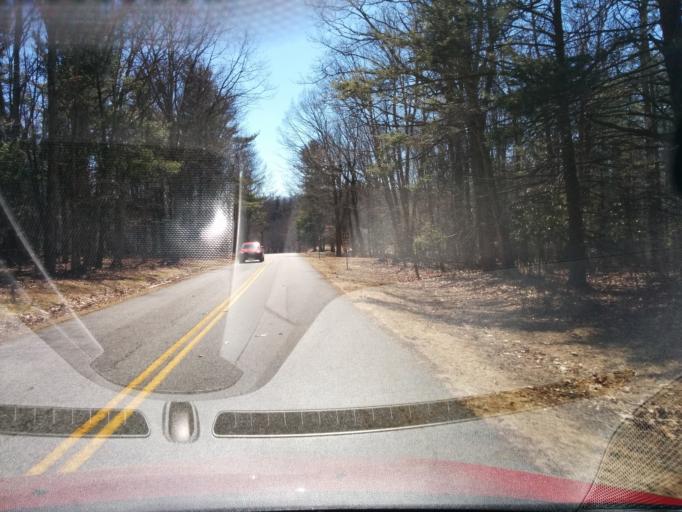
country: US
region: Virginia
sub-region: Augusta County
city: Stuarts Draft
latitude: 37.8702
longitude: -79.1471
